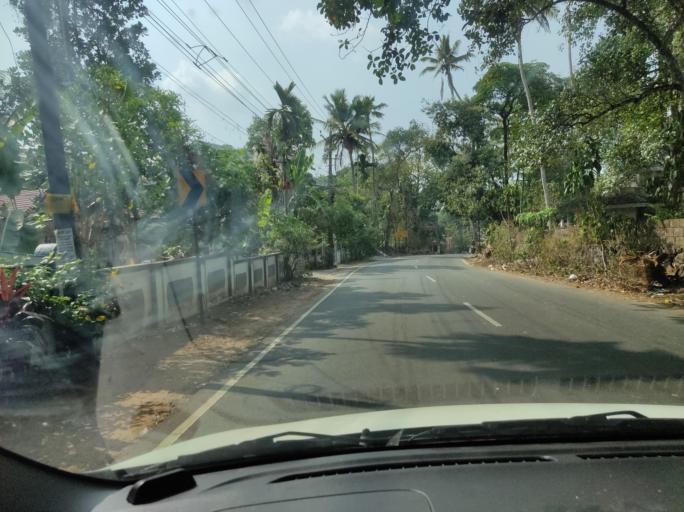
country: IN
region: Kerala
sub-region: Kottayam
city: Kottayam
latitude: 9.6786
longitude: 76.5095
